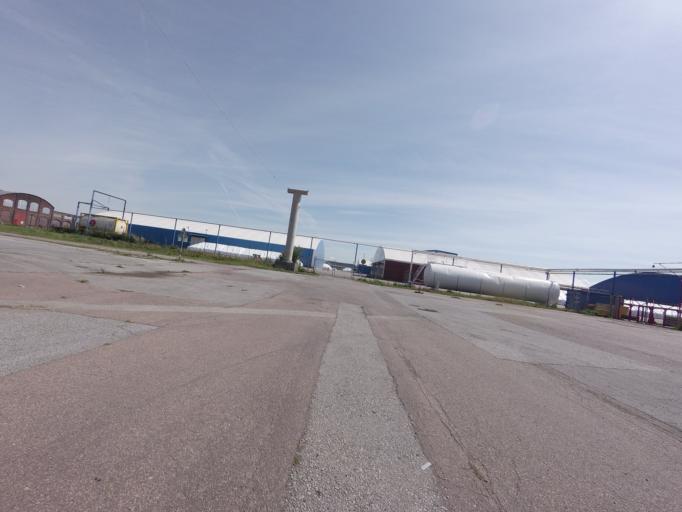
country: SE
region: Skane
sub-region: Landskrona
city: Landskrona
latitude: 55.8622
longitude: 12.8311
